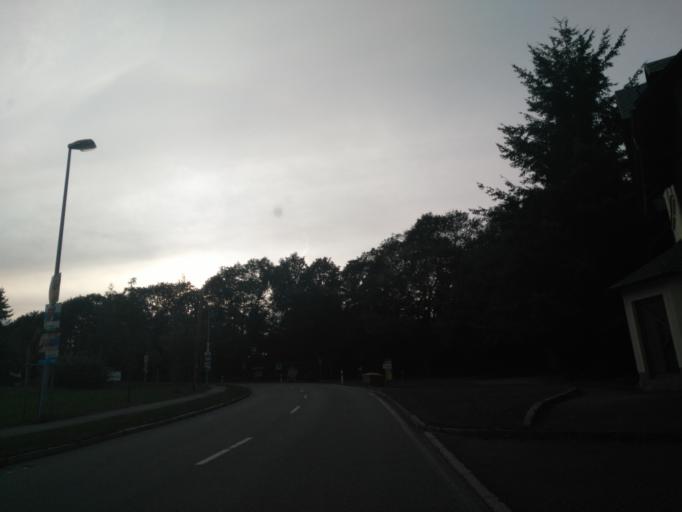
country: DE
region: Saxony
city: Geyer
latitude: 50.6259
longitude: 12.9367
